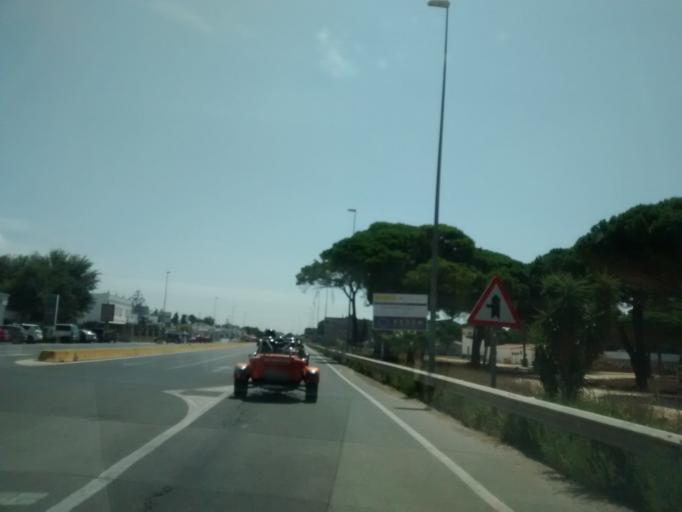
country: ES
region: Andalusia
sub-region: Provincia de Cadiz
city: Conil de la Frontera
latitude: 36.3345
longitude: -6.0917
